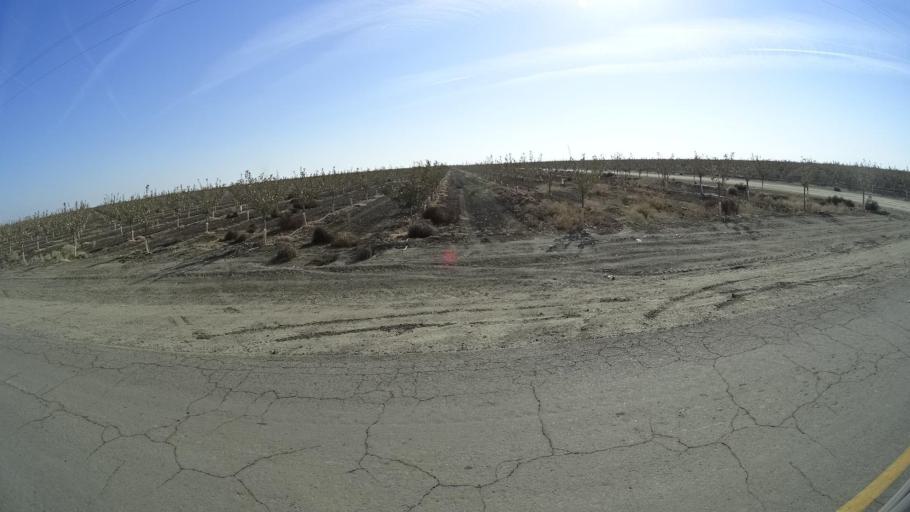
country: US
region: California
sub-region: Kern County
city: Wasco
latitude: 35.7032
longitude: -119.4101
